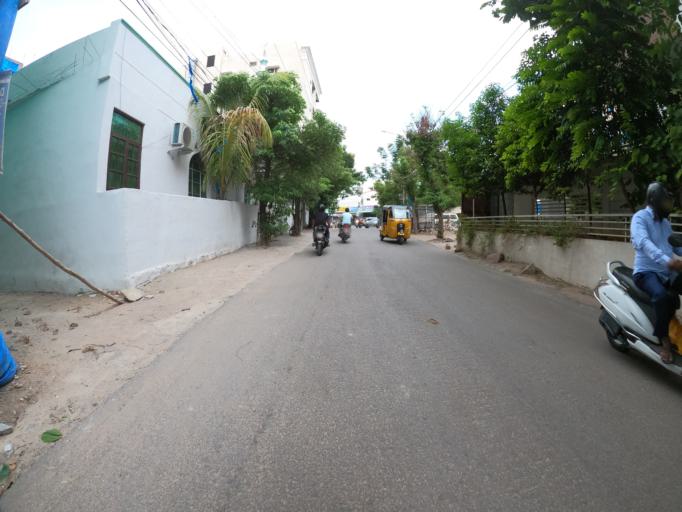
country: IN
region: Telangana
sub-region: Hyderabad
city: Hyderabad
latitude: 17.4070
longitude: 78.3916
